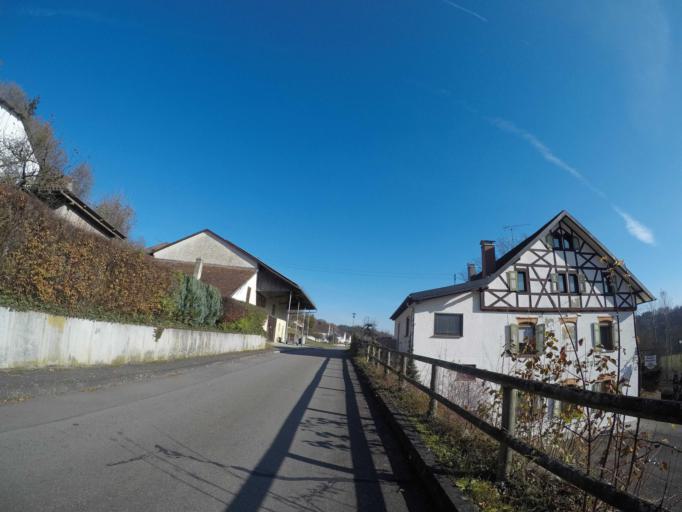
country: DE
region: Baden-Wuerttemberg
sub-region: Tuebingen Region
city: Rechtenstein
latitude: 48.2407
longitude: 9.5511
